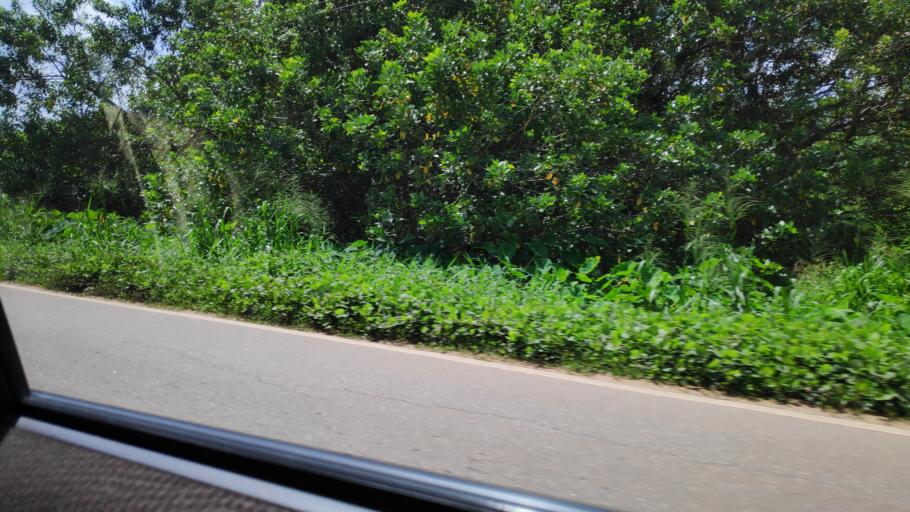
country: LK
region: Western
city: Minuwangoda
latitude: 7.2814
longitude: 80.0527
